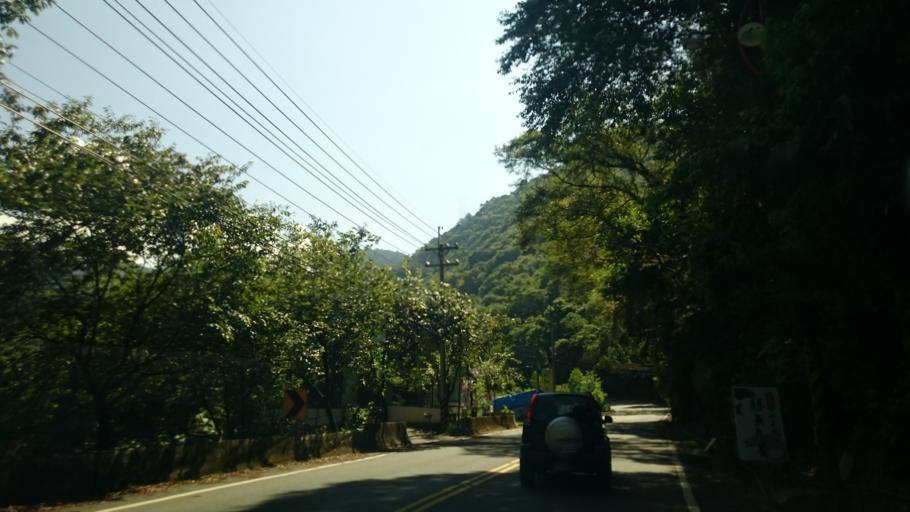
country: TW
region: Taiwan
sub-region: Nantou
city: Puli
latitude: 24.0076
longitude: 121.0953
